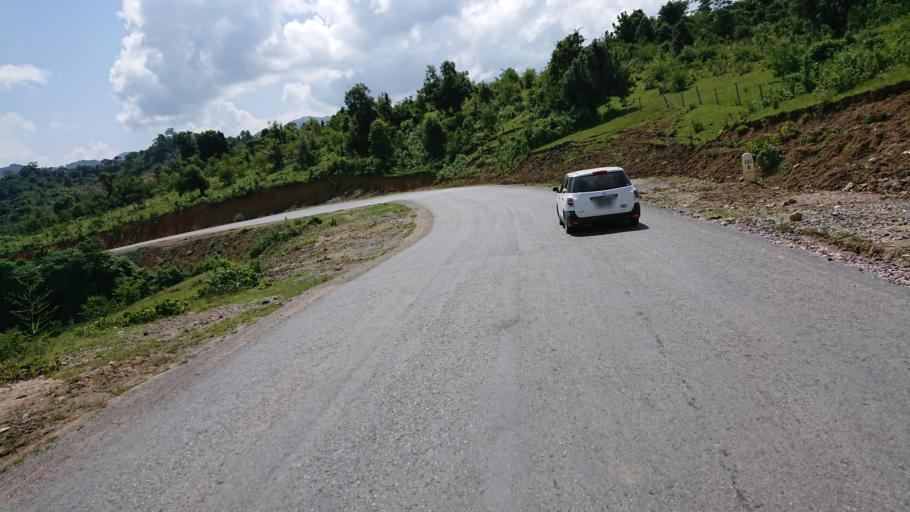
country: MM
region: Shan
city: Taunggyi
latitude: 20.8181
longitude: 97.3130
